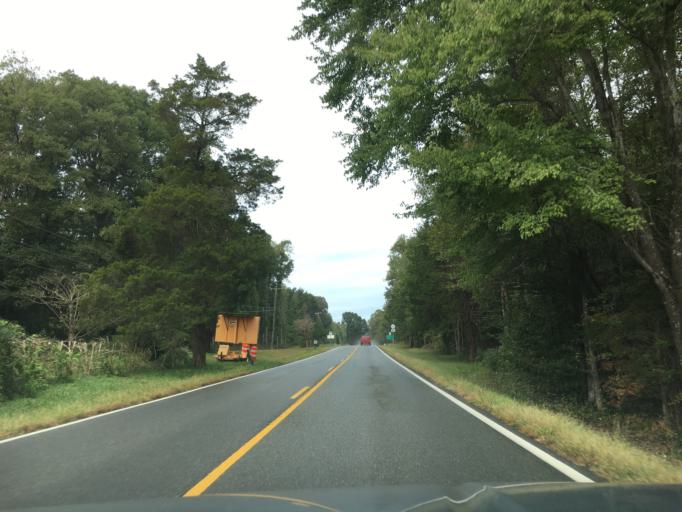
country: US
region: Virginia
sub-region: Goochland County
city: Goochland
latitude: 37.7306
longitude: -77.8361
